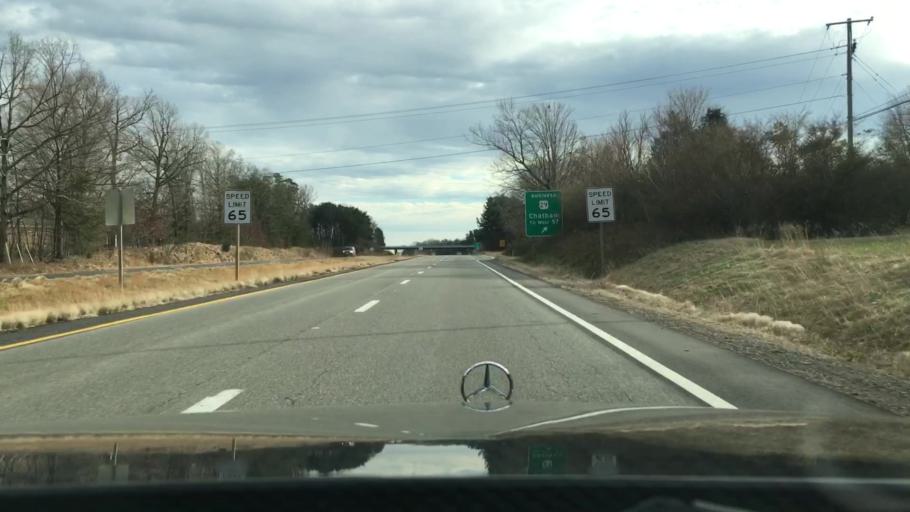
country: US
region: Virginia
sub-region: Pittsylvania County
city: Chatham
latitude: 36.8528
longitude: -79.3959
